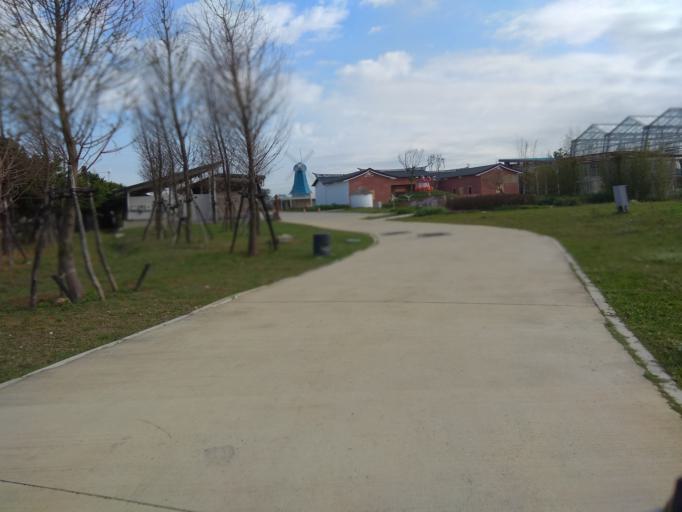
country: TW
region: Taiwan
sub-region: Hsinchu
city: Zhubei
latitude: 25.0062
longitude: 121.0480
